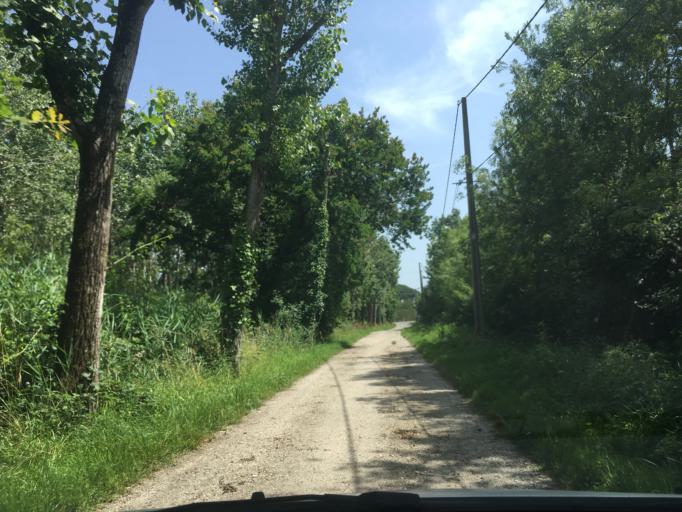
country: FR
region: Aquitaine
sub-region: Departement de la Gironde
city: Cantenac
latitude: 45.0249
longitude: -0.6380
